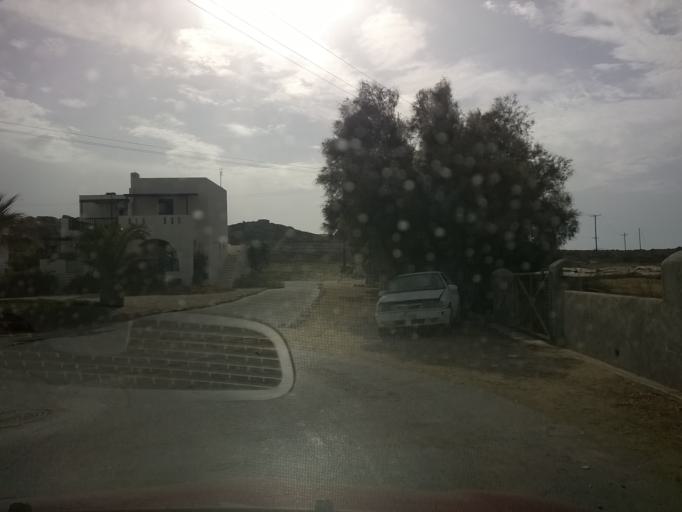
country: GR
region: South Aegean
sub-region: Nomos Kykladon
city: Naxos
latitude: 37.0805
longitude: 25.3426
